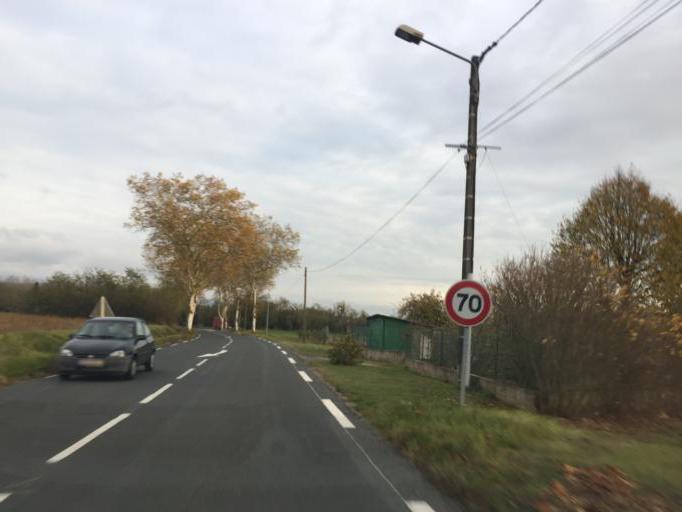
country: FR
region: Rhone-Alpes
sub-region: Departement de l'Ain
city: Meximieux
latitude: 45.9220
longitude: 5.2293
